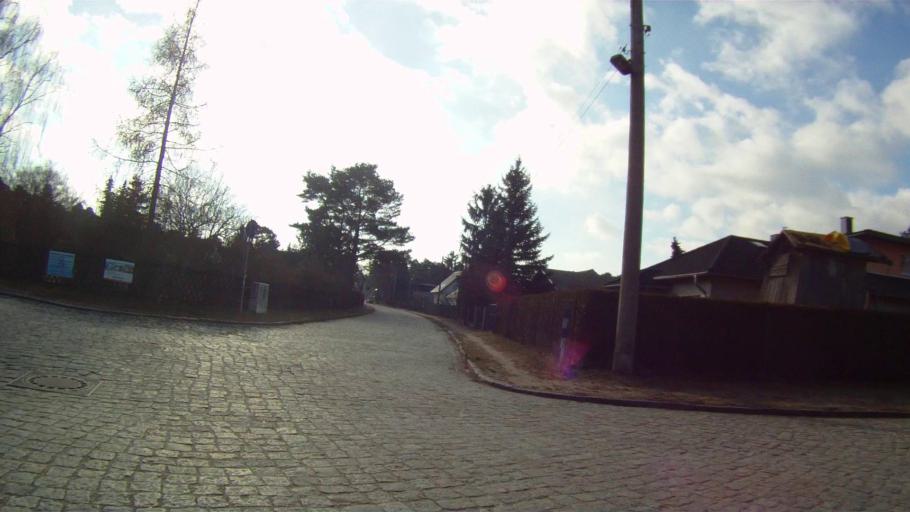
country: DE
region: Berlin
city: Mahlsdorf
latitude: 52.4802
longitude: 13.6163
